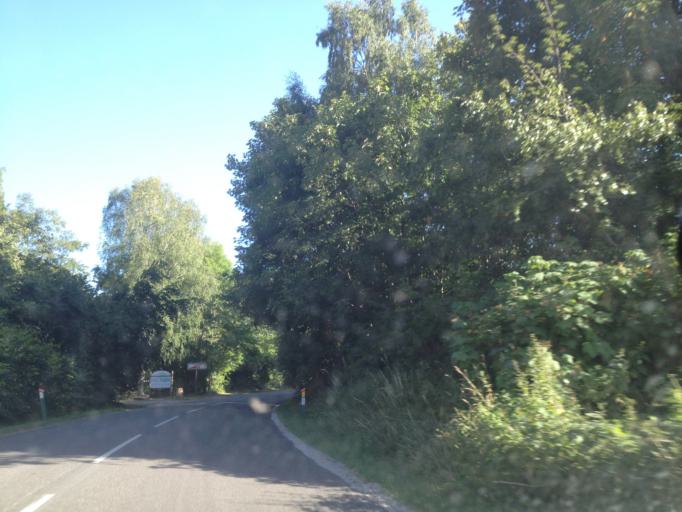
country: DK
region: Capital Region
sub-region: Gribskov Kommune
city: Helsinge
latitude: 56.0472
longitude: 12.1102
